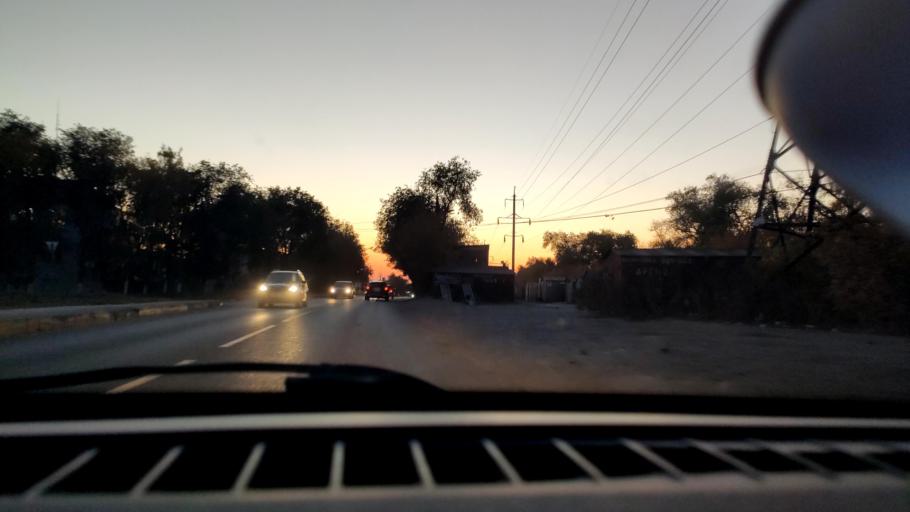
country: RU
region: Samara
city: Samara
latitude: 53.1842
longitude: 50.1715
